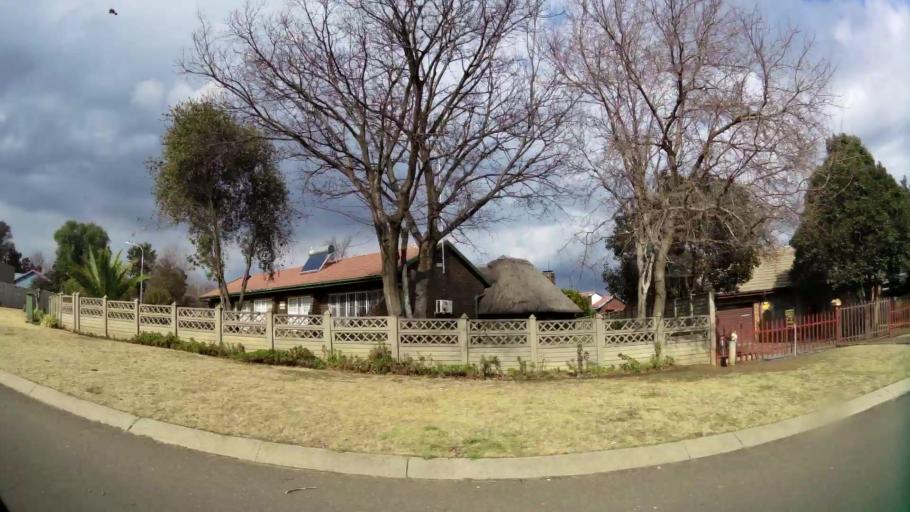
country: ZA
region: Gauteng
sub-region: Sedibeng District Municipality
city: Vanderbijlpark
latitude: -26.7080
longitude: 27.8029
